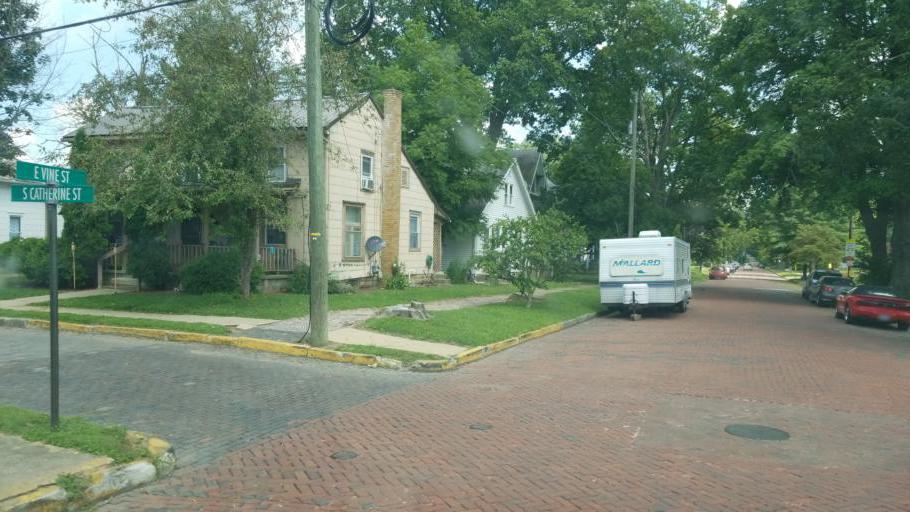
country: US
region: Ohio
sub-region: Knox County
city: Mount Vernon
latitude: 40.3921
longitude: -82.4742
